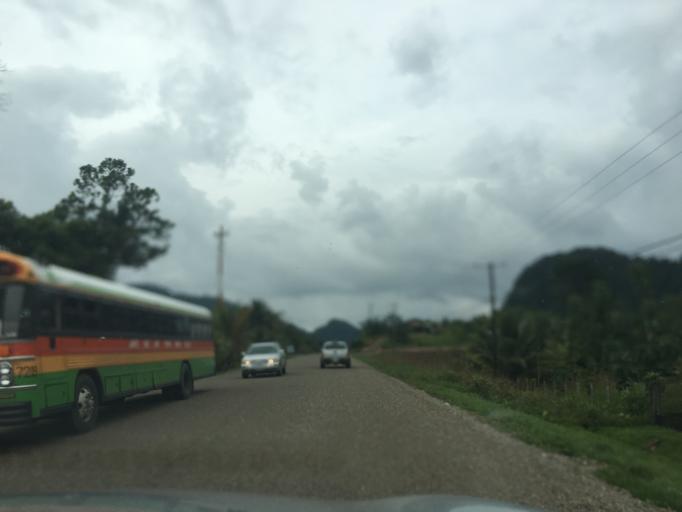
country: BZ
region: Cayo
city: Belmopan
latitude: 17.0882
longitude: -88.6115
